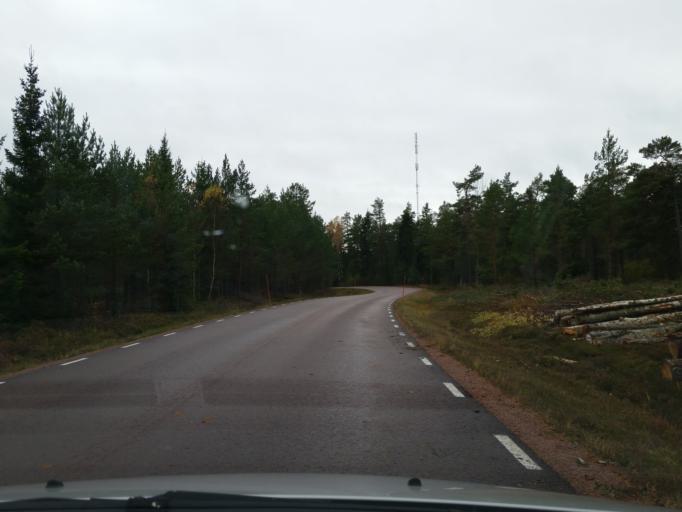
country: AX
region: Alands landsbygd
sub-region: Lemland
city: Lemland
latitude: 60.0635
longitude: 20.1627
